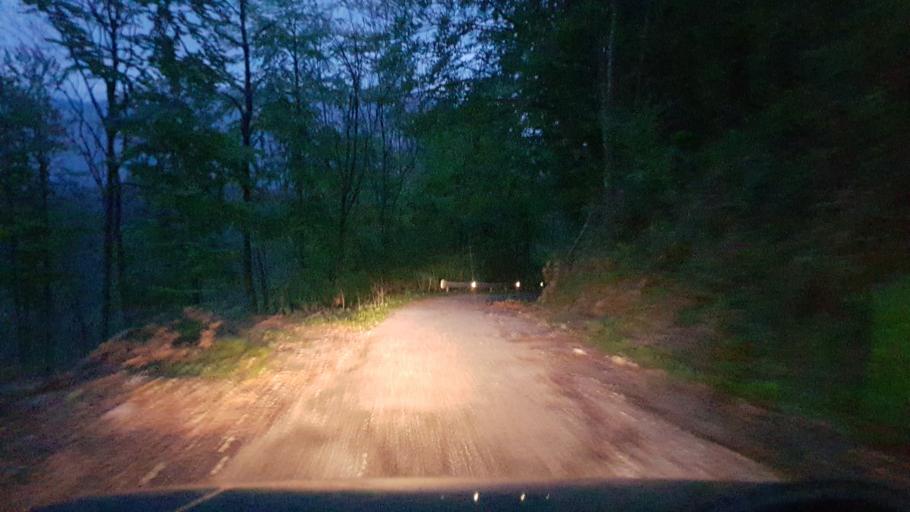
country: IT
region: Friuli Venezia Giulia
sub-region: Provincia di Udine
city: Taipana
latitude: 46.2485
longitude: 13.3565
